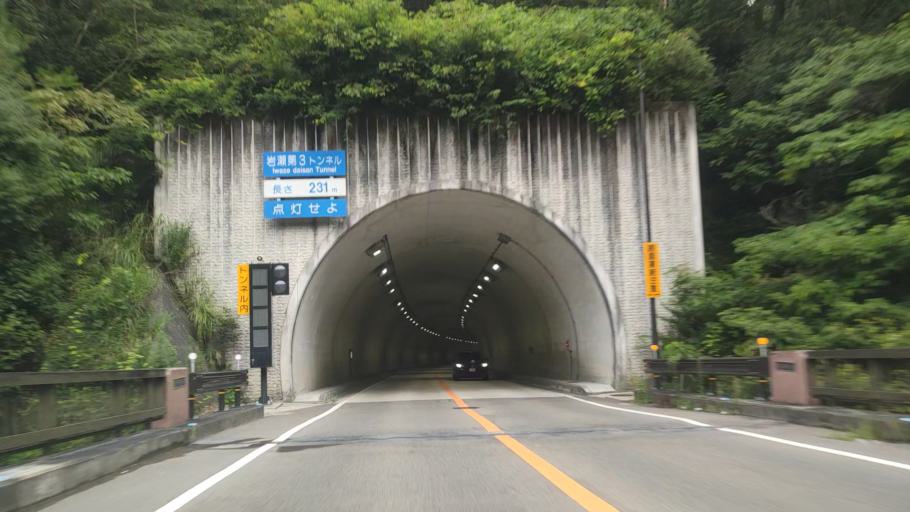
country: JP
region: Wakayama
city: Hashimoto
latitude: 34.4065
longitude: 135.5931
